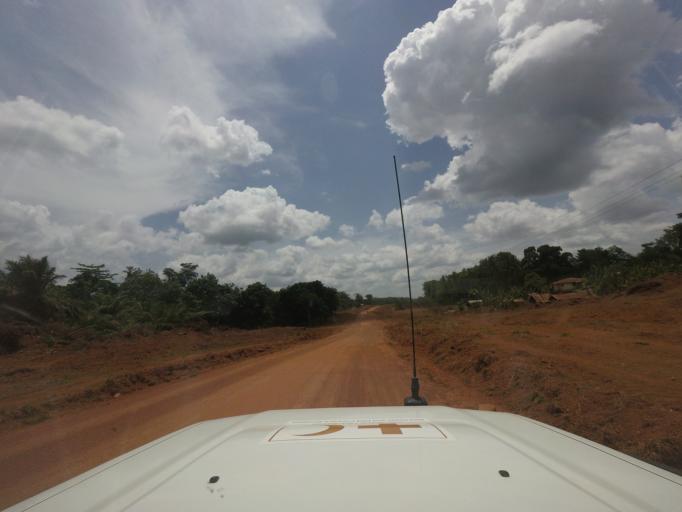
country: LR
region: Nimba
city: Sanniquellie
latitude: 7.2313
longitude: -8.9110
